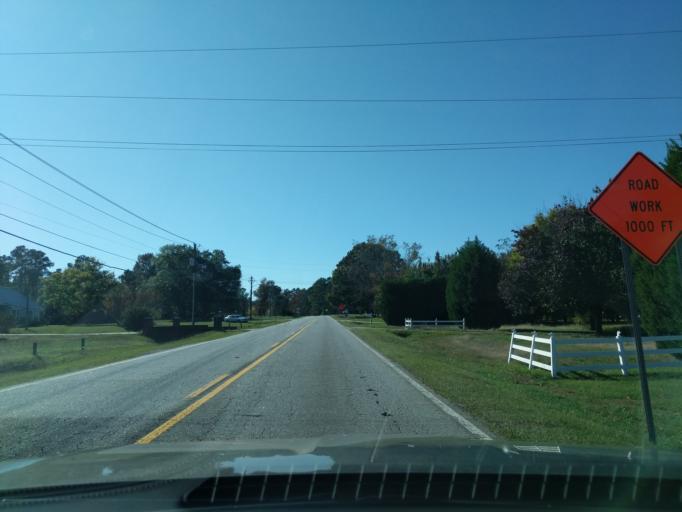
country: US
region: Georgia
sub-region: Columbia County
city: Grovetown
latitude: 33.4653
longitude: -82.1709
